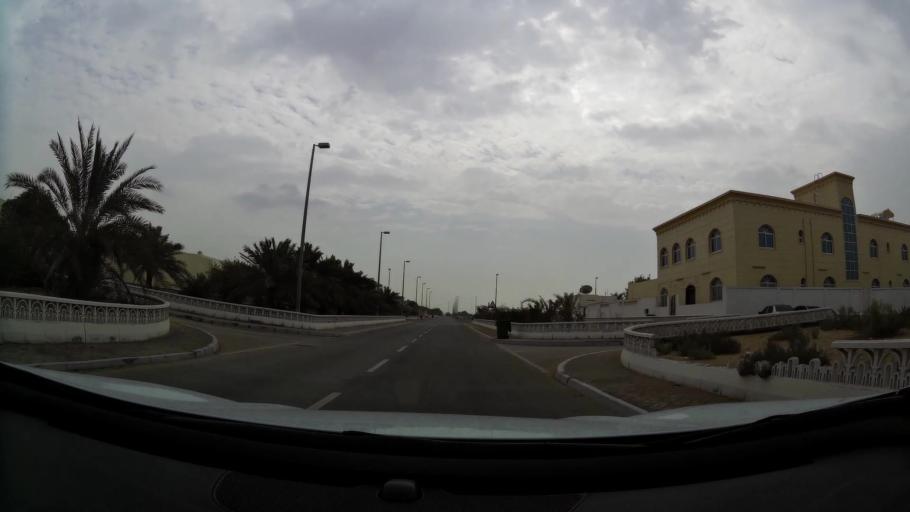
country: AE
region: Abu Dhabi
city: Abu Dhabi
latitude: 24.6291
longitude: 54.7121
